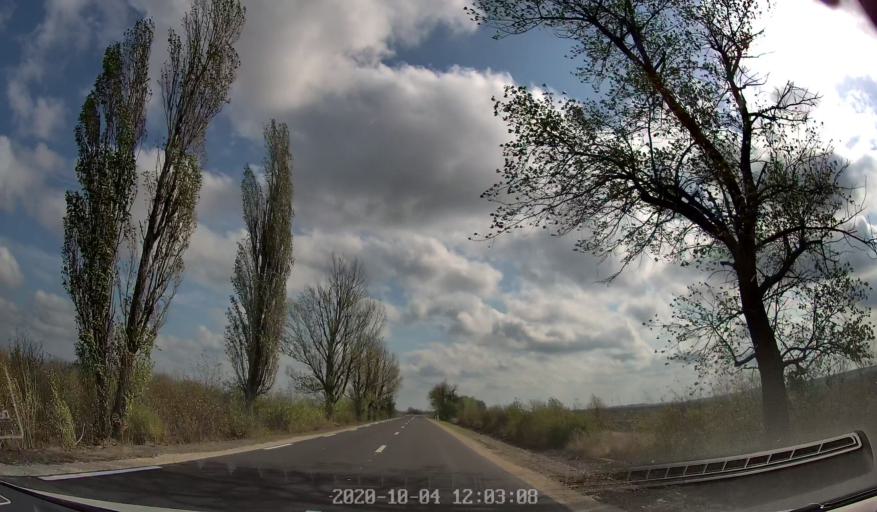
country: MD
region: Rezina
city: Saharna
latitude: 47.6136
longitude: 28.9211
